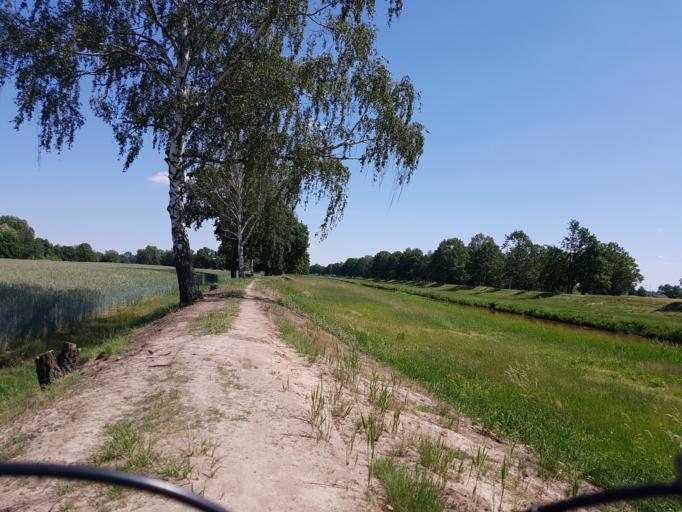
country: DE
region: Brandenburg
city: Elsterwerda
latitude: 51.4595
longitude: 13.4908
